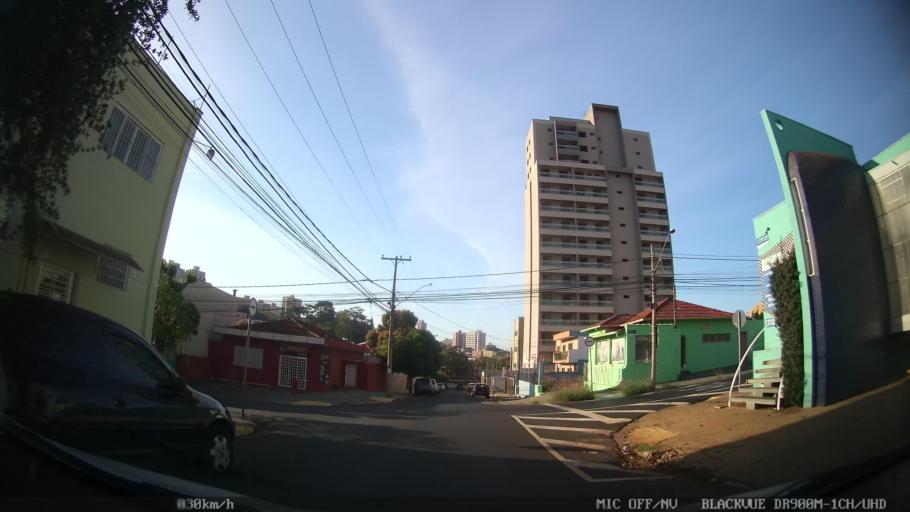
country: BR
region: Sao Paulo
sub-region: Ribeirao Preto
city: Ribeirao Preto
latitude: -21.1841
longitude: -47.8005
